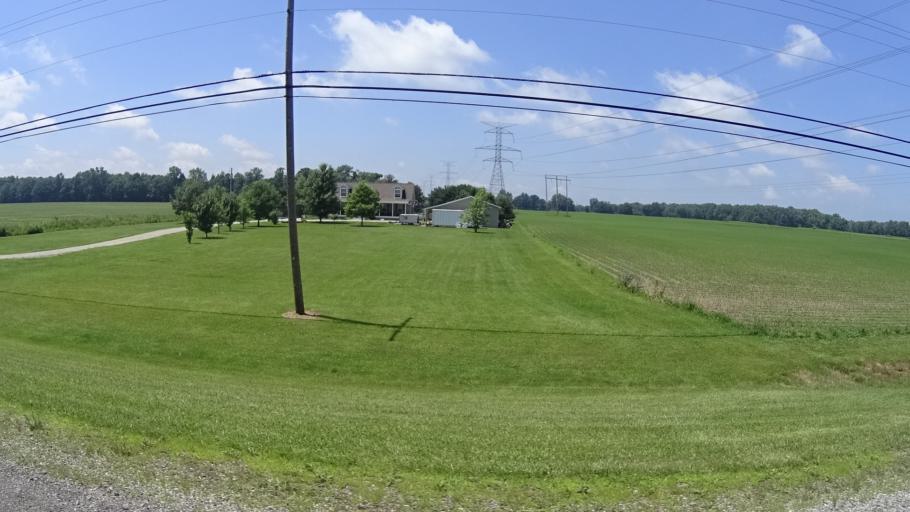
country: US
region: Ohio
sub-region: Lorain County
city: Vermilion
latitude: 41.3433
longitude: -82.3599
